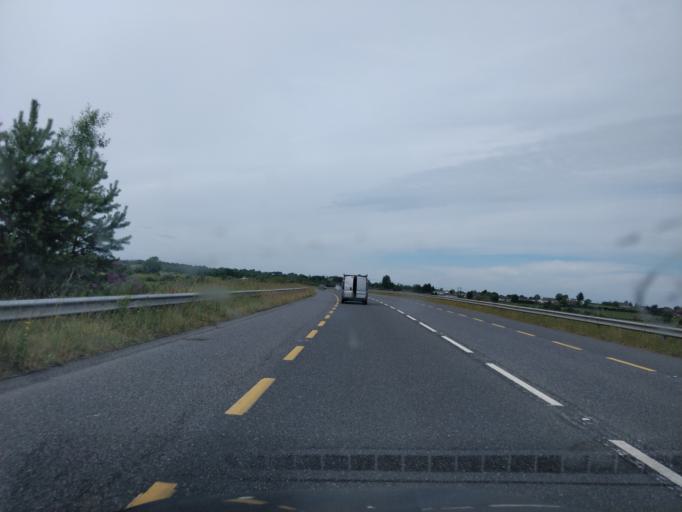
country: IE
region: Leinster
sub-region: Uibh Fhaili
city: Tullamore
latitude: 53.2801
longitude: -7.4696
